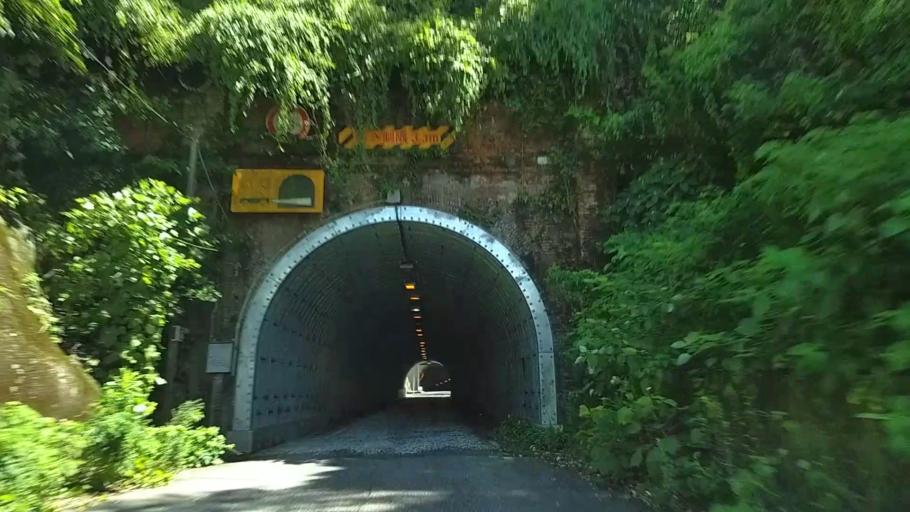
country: JP
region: Kanagawa
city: Kamakura
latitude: 35.3082
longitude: 139.5621
